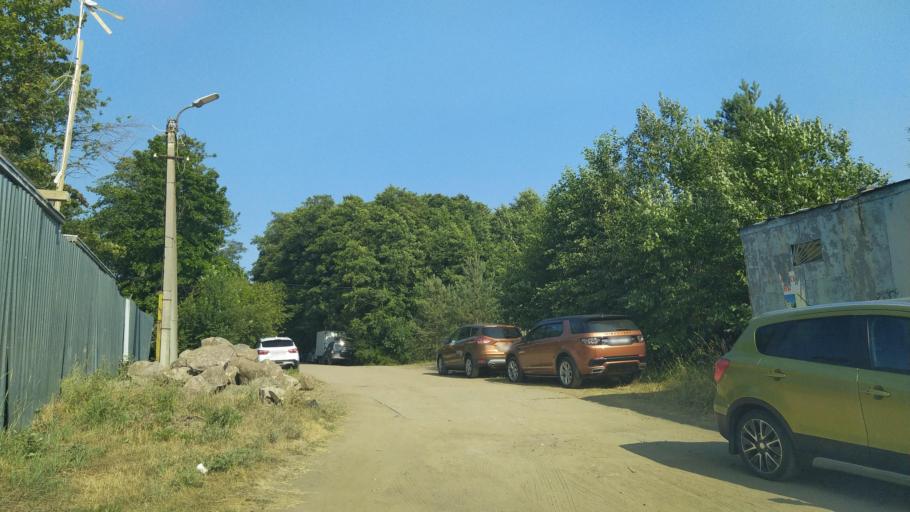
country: RU
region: Leningrad
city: Gorskaya
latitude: 60.0568
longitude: 29.9673
